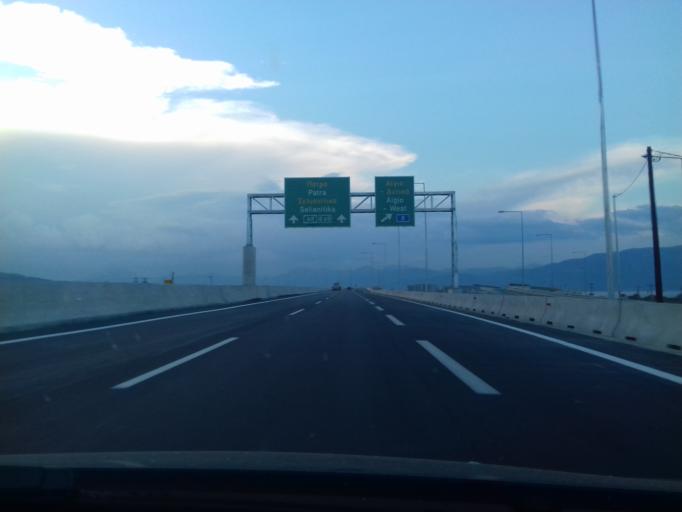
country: GR
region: West Greece
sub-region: Nomos Achaias
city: Aigio
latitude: 38.2600
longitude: 22.0612
